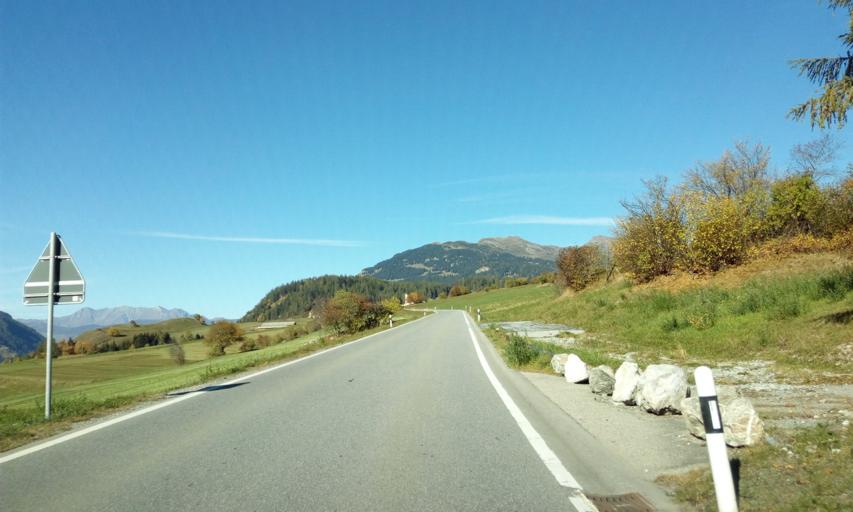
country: CH
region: Grisons
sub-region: Albula District
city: Tiefencastel
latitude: 46.6761
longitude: 9.5761
